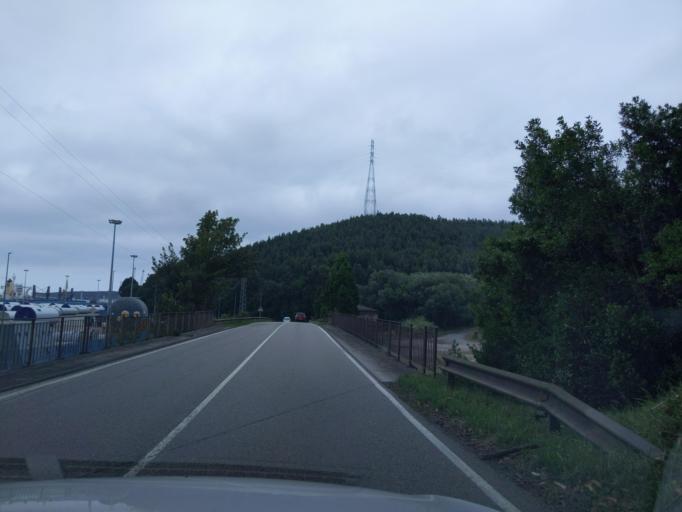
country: ES
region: Asturias
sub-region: Province of Asturias
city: Aviles
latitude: 43.5683
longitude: -5.9153
